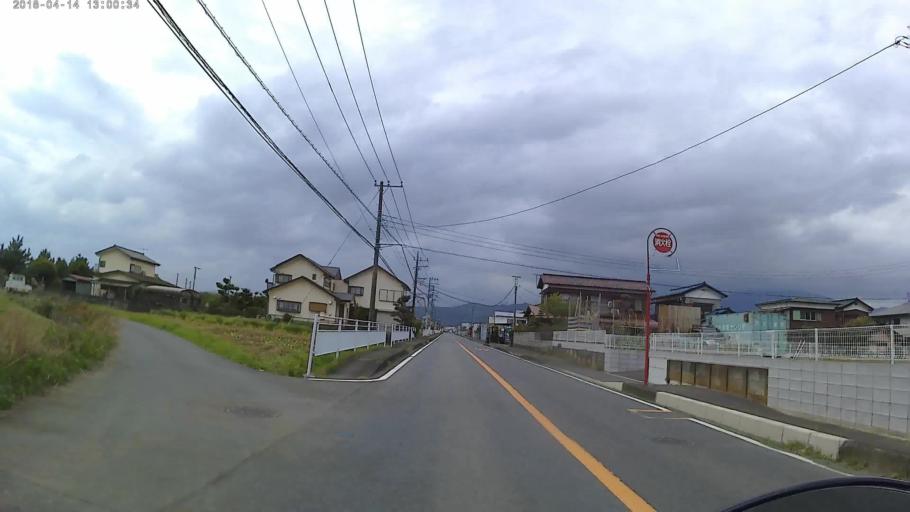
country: JP
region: Kanagawa
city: Isehara
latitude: 35.3727
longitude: 139.3038
